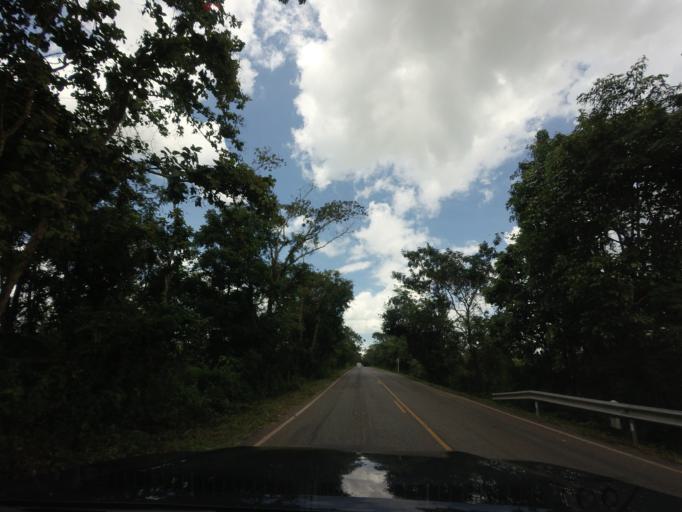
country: TH
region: Changwat Udon Thani
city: Phibun Rak
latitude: 17.6110
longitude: 103.0788
